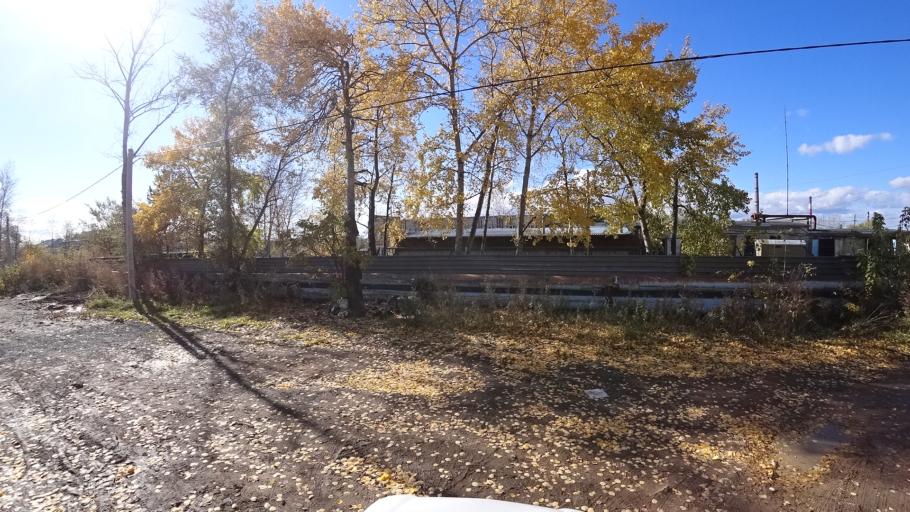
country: RU
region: Khabarovsk Krai
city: Amursk
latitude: 50.2199
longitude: 136.9024
